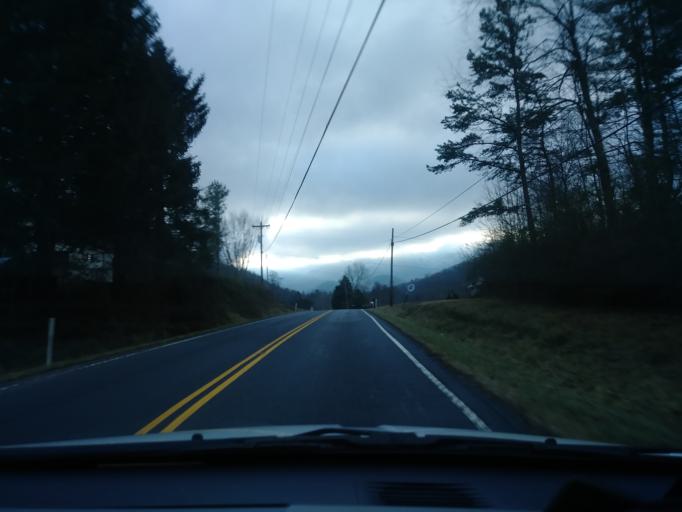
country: US
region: Tennessee
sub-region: Unicoi County
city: Unicoi
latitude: 36.1857
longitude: -82.3288
